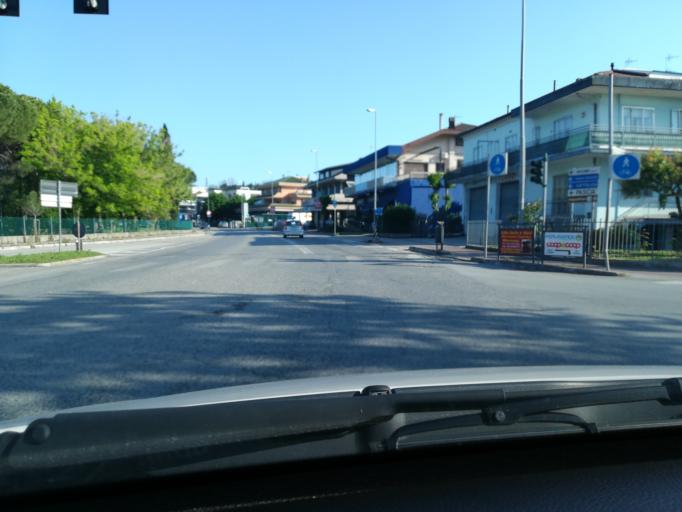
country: IT
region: Emilia-Romagna
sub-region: Provincia di Rimini
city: Riccione
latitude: 43.9951
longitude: 12.6487
